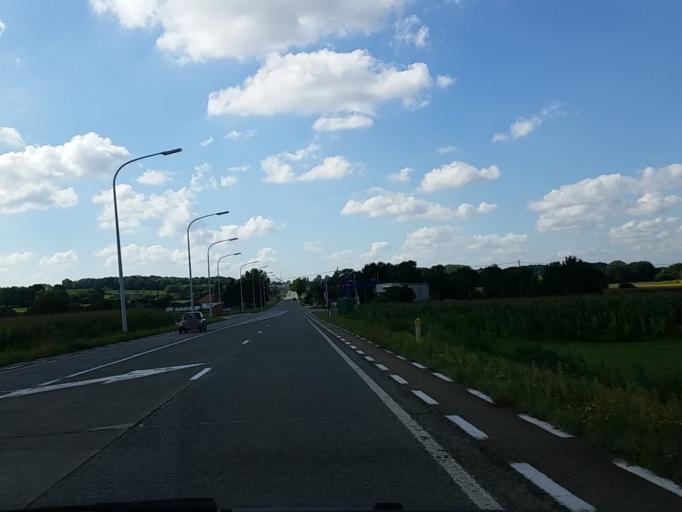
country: BE
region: Flanders
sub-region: Provincie Vlaams-Brabant
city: Bekkevoort
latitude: 50.9340
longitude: 4.9396
